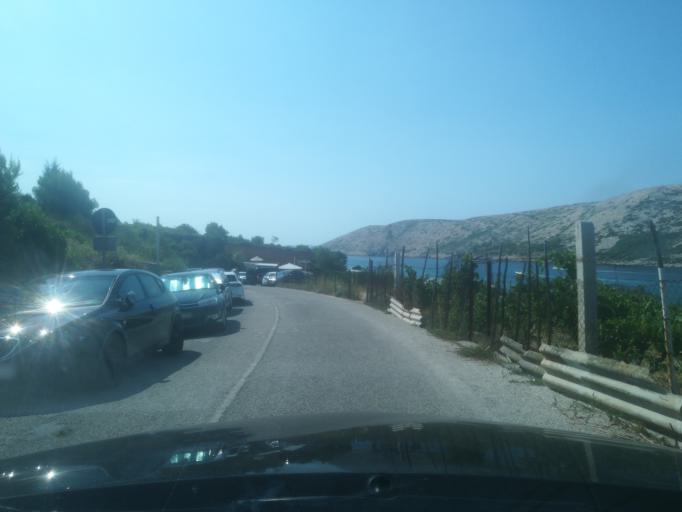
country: HR
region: Primorsko-Goranska
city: Banjol
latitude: 44.7087
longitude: 14.8308
